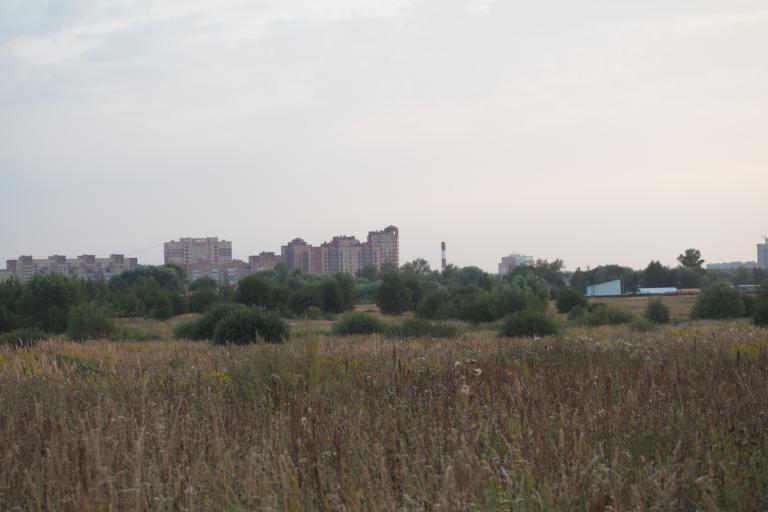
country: RU
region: Moskovskaya
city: Ramenskoye
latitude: 55.5888
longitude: 38.2624
